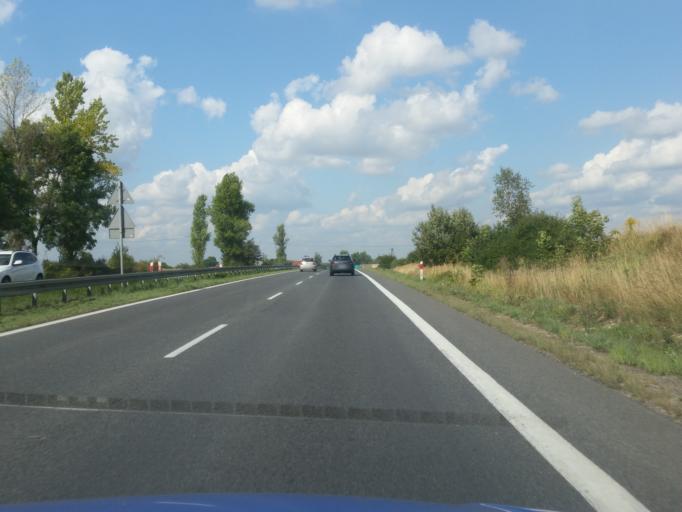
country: PL
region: Silesian Voivodeship
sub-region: Powiat bedzinski
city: Siewierz
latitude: 50.5007
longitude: 19.2008
